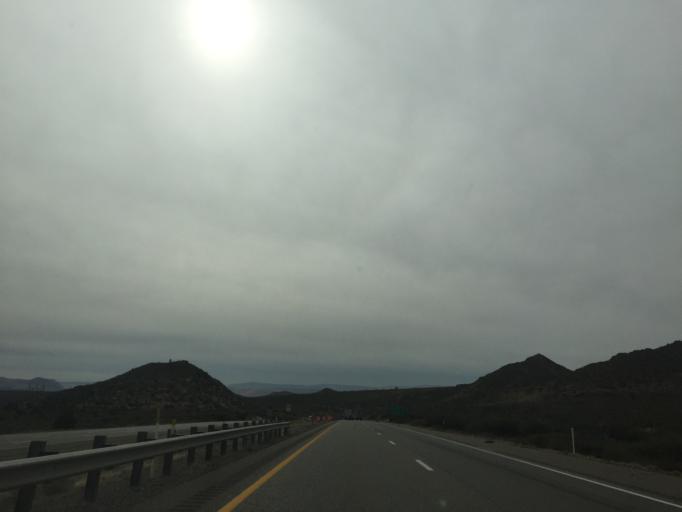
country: US
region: Utah
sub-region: Washington County
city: Toquerville
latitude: 37.3164
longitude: -113.2921
